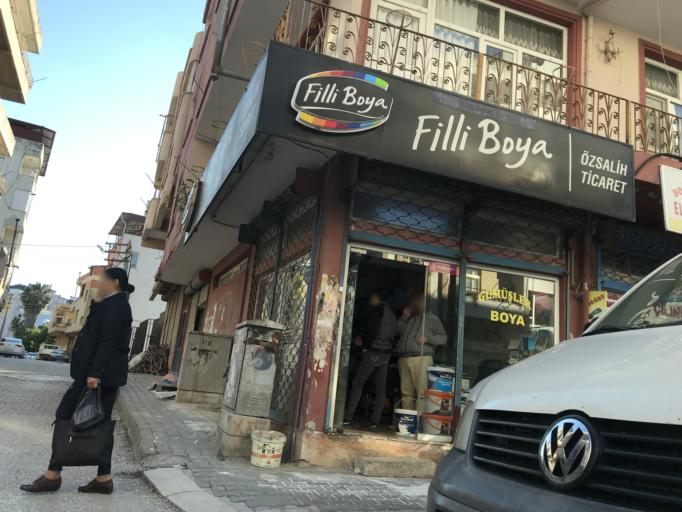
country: TR
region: Hatay
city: Samandag
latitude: 36.0830
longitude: 35.9831
